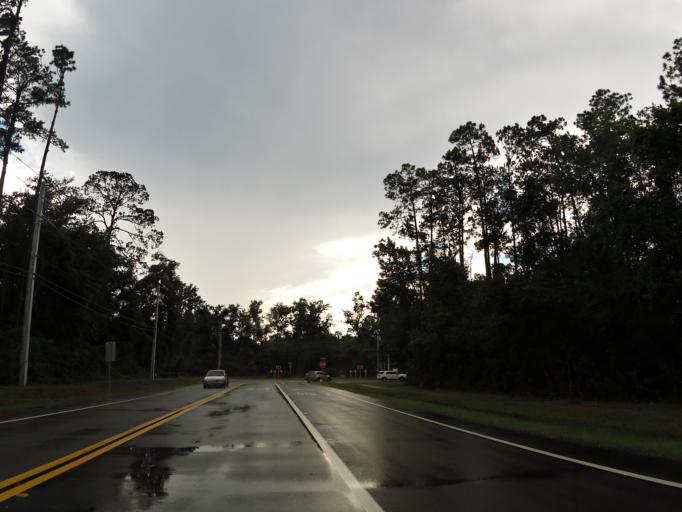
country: US
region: Florida
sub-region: Saint Johns County
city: Fruit Cove
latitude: 30.0643
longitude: -81.6607
